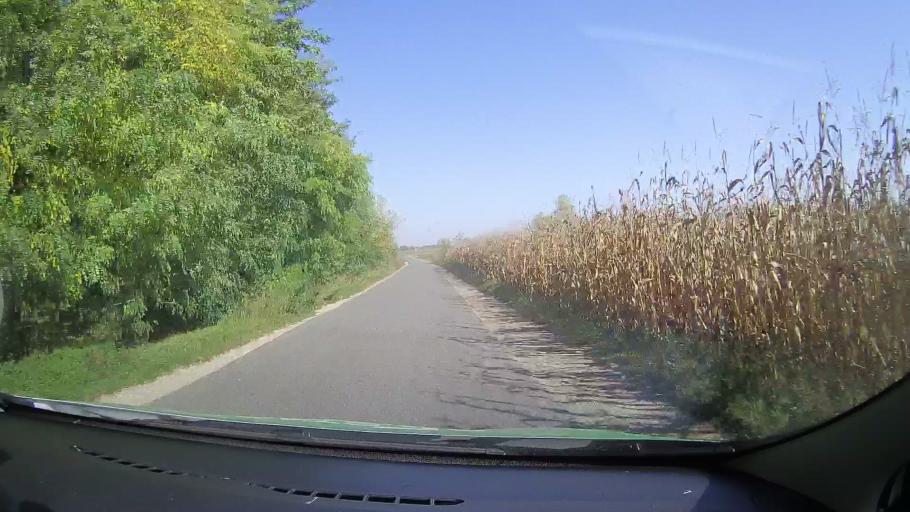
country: RO
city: Foieni
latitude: 47.6907
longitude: 22.3554
